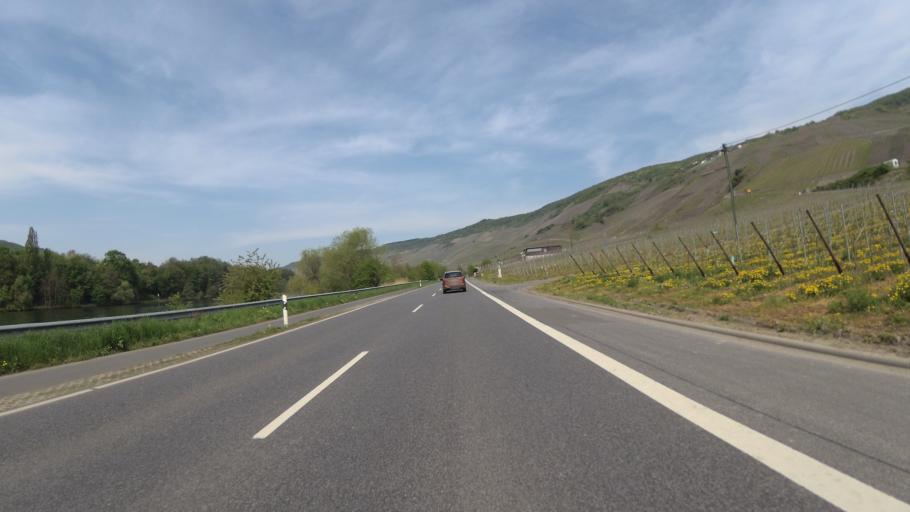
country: DE
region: Rheinland-Pfalz
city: Bernkastel-Kues
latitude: 49.9258
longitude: 7.0685
